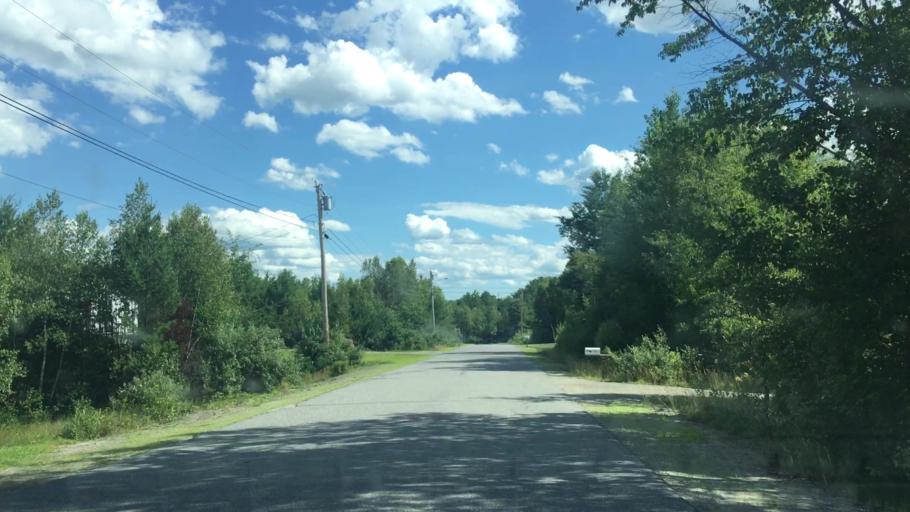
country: US
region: Maine
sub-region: Franklin County
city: Farmington
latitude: 44.6708
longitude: -70.1309
